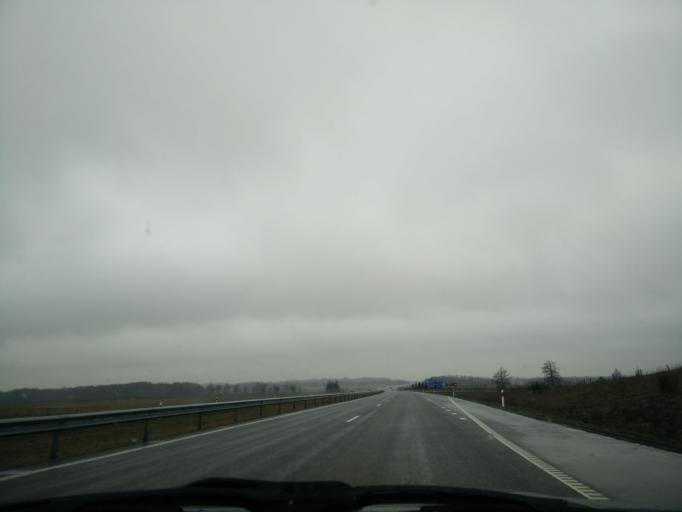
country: LT
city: Skaudvile
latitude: 55.4831
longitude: 22.5915
